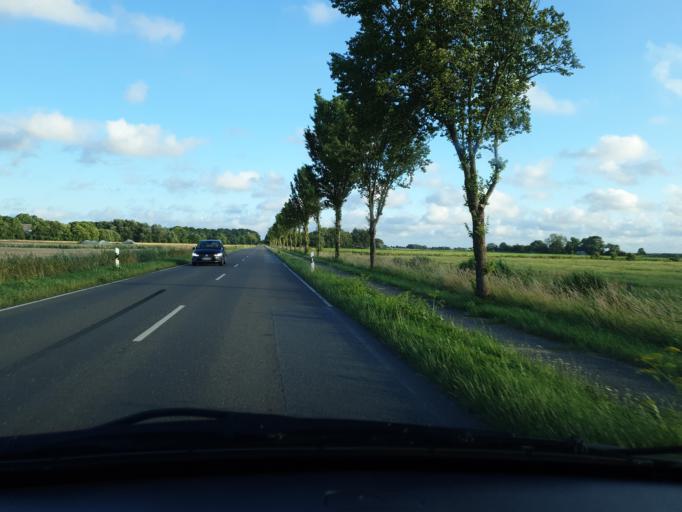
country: DE
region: Schleswig-Holstein
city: Wohrden
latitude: 54.1372
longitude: 9.0166
